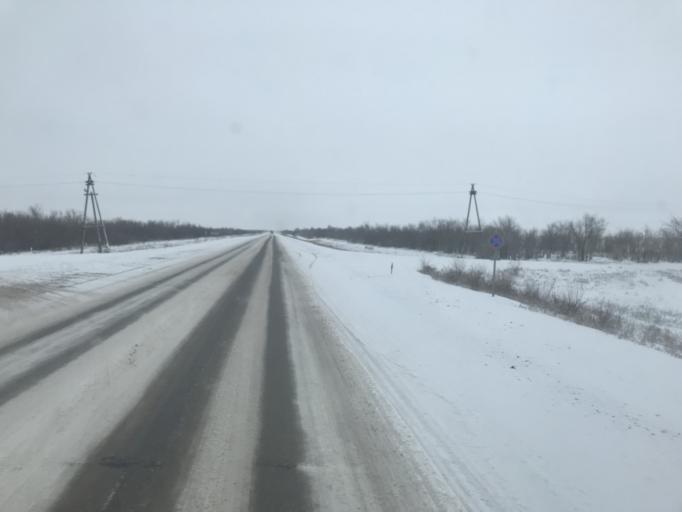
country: KZ
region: Batys Qazaqstan
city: Oral
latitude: 51.0502
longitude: 51.5702
